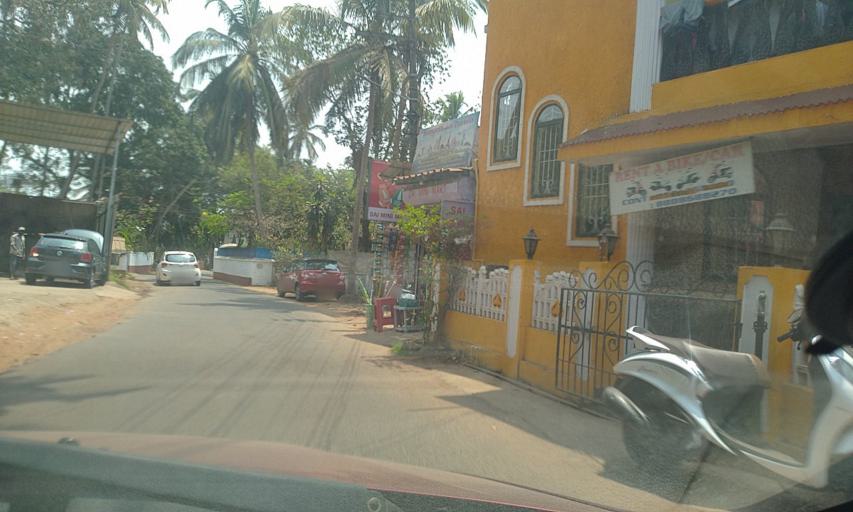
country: IN
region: Goa
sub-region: North Goa
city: Saligao
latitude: 15.5519
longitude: 73.7824
